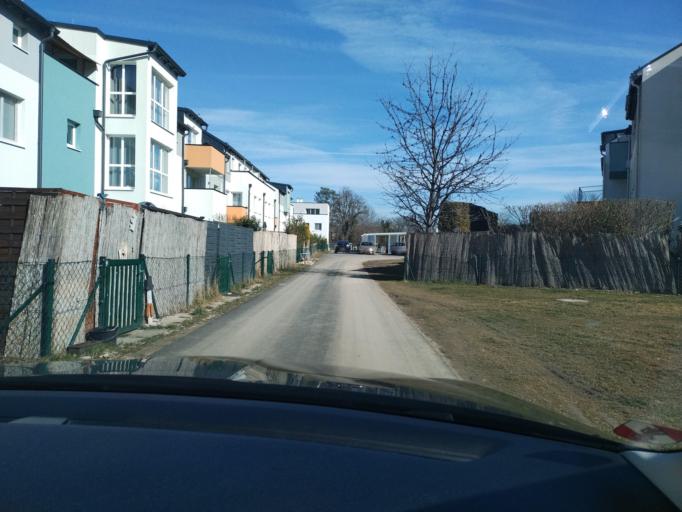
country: AT
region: Lower Austria
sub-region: Politischer Bezirk Neunkirchen
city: Pitten
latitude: 47.7257
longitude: 16.1700
